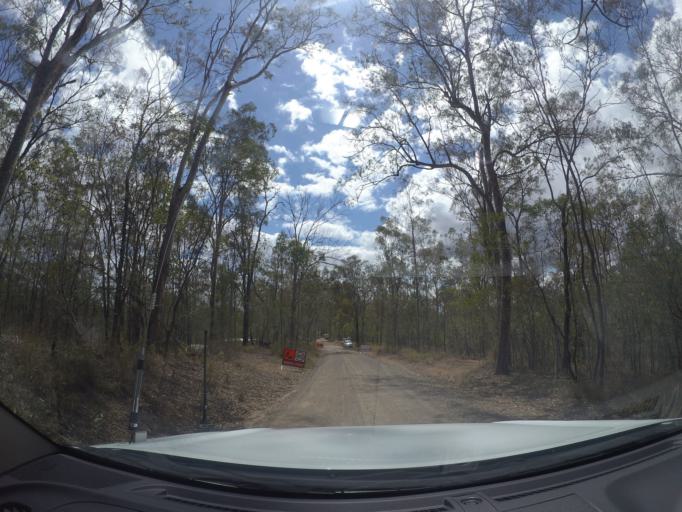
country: AU
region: Queensland
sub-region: Logan
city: Cedar Vale
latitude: -27.8884
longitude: 153.0427
